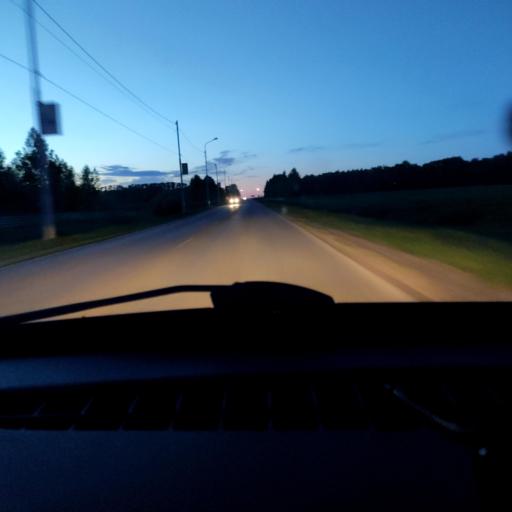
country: RU
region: Bashkortostan
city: Karmaskaly
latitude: 54.3786
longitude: 56.1770
